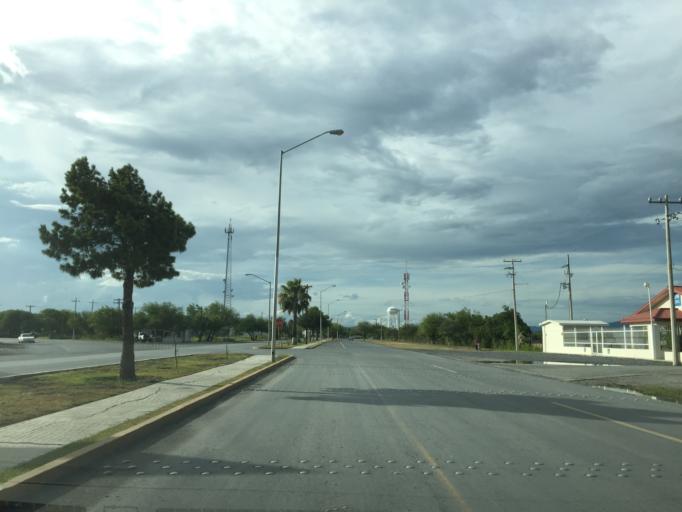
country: MX
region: Nuevo Leon
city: Marin
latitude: 25.8684
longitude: -100.0256
